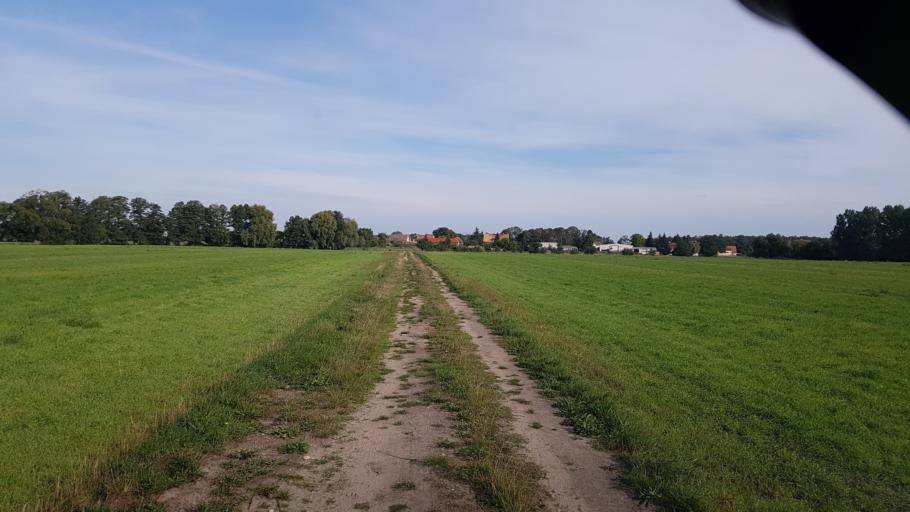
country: DE
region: Brandenburg
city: Finsterwalde
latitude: 51.6587
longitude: 13.6832
